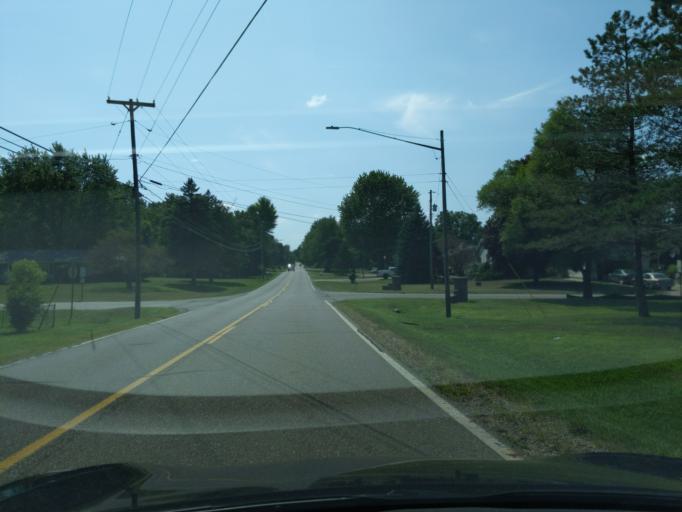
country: US
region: Michigan
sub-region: Eaton County
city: Grand Ledge
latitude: 42.7503
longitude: -84.7203
